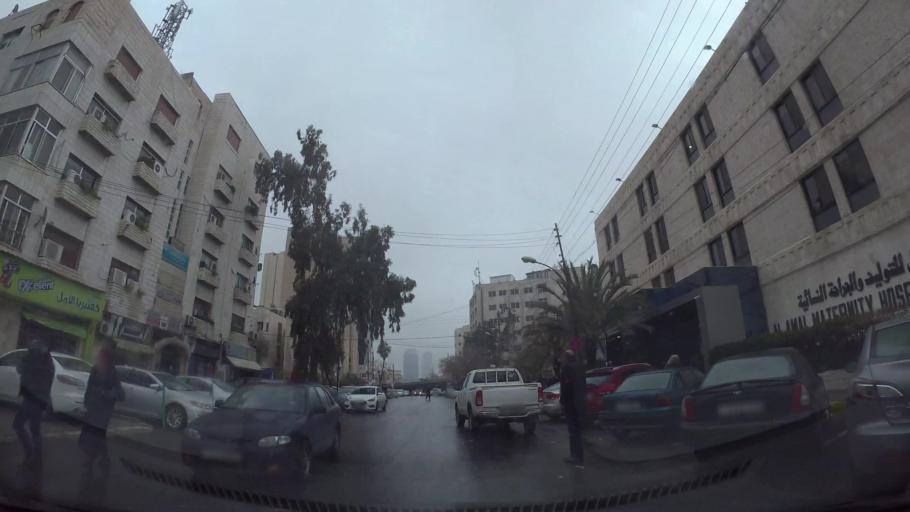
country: JO
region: Amman
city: Amman
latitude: 31.9735
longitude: 35.9112
